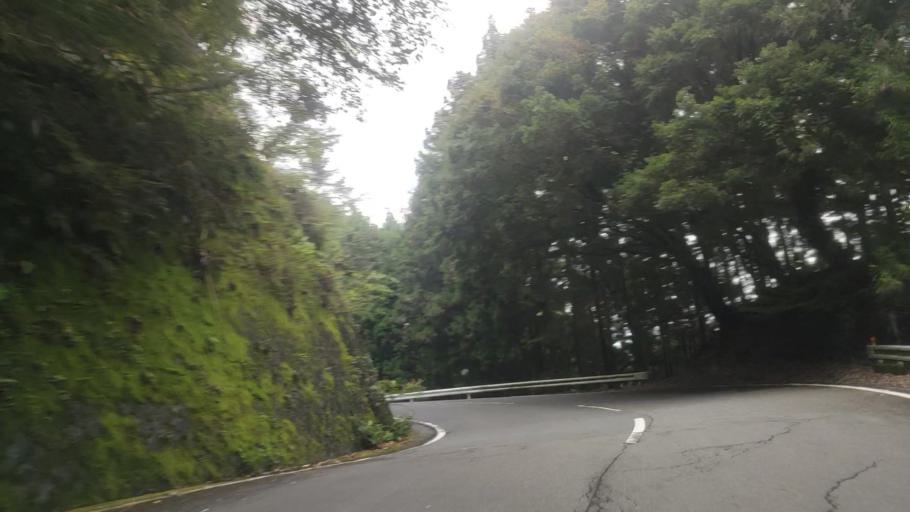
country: JP
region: Wakayama
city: Koya
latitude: 34.2116
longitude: 135.5434
